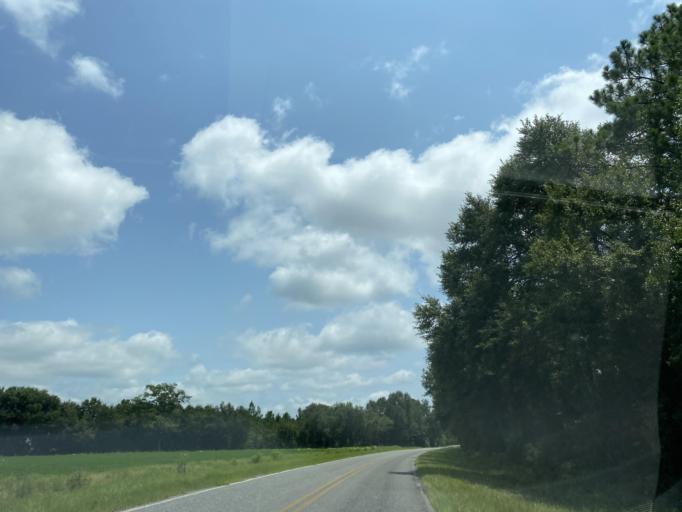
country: US
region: Georgia
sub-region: Telfair County
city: Lumber City
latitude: 32.0014
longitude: -82.7119
